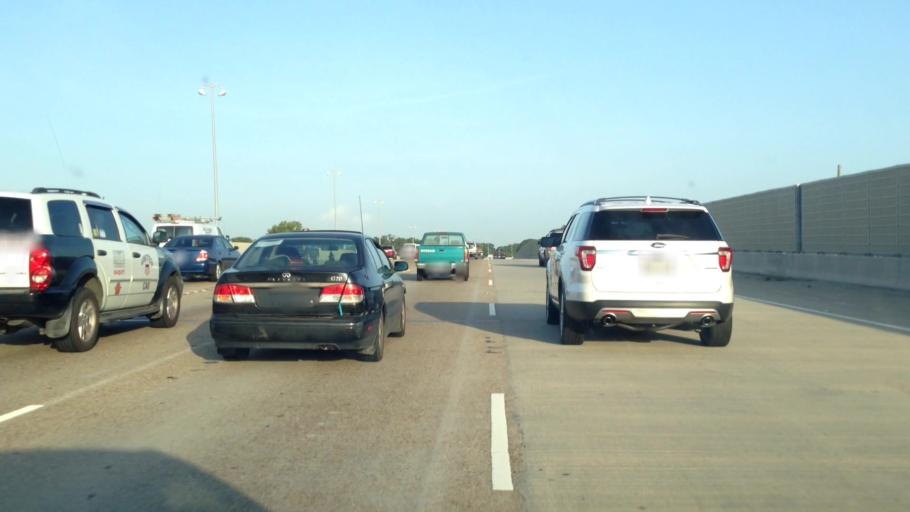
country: US
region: Louisiana
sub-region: Jefferson Parish
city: Metairie Terrace
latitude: 29.9998
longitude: -90.1921
